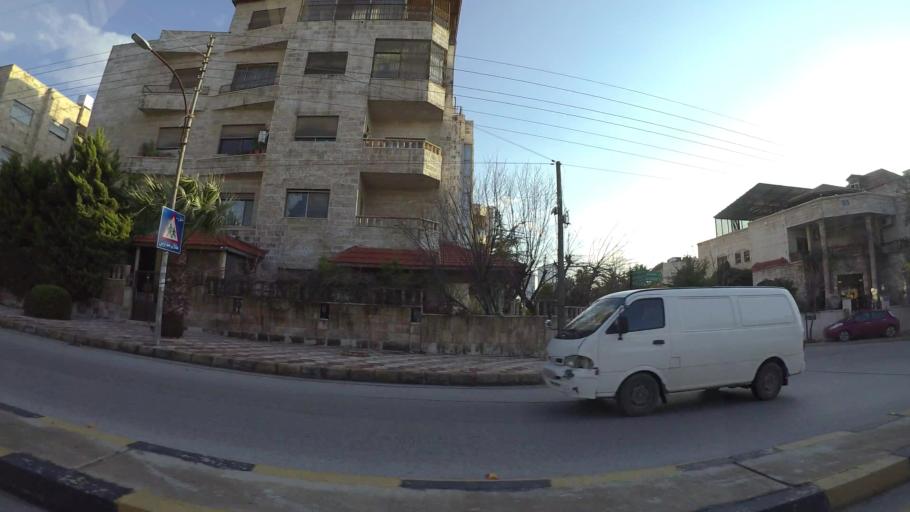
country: JO
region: Amman
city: Al Jubayhah
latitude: 31.9743
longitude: 35.8753
